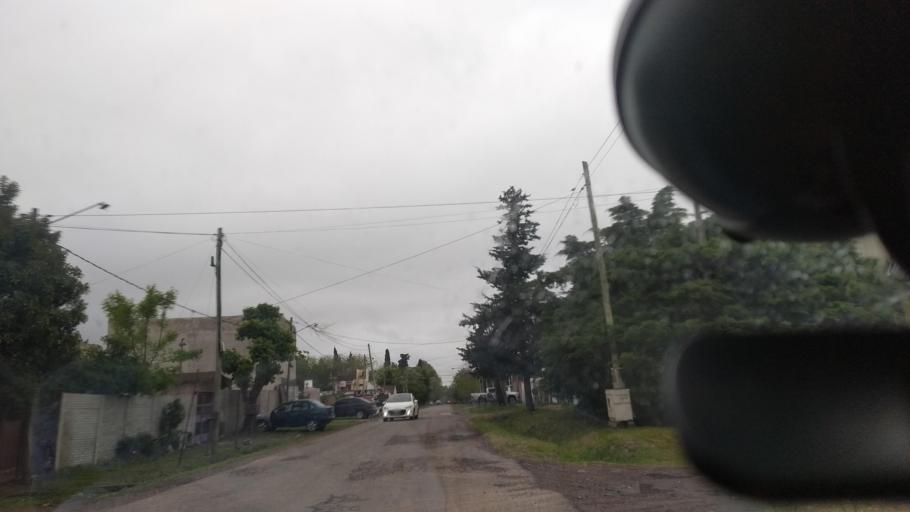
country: AR
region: Buenos Aires
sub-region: Partido de La Plata
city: La Plata
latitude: -34.9559
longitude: -57.9986
